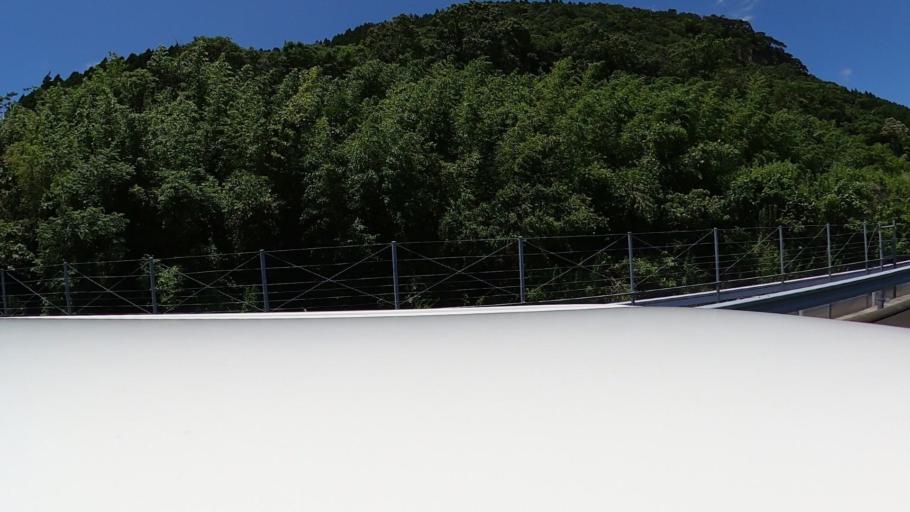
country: JP
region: Miyazaki
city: Nobeoka
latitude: 32.3894
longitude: 131.6221
